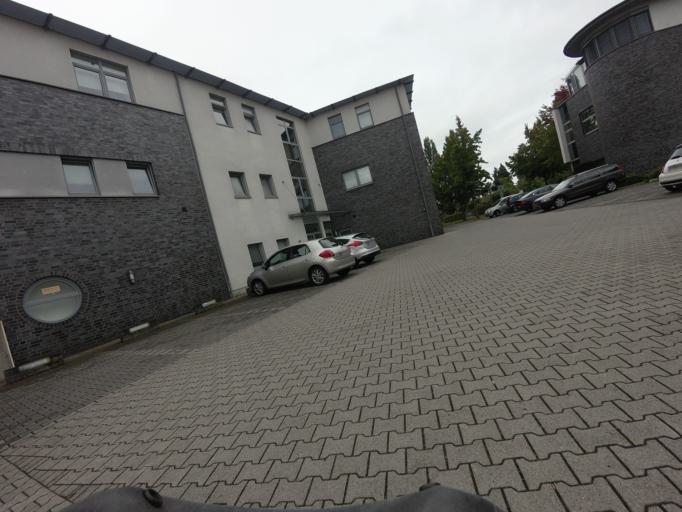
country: DE
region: North Rhine-Westphalia
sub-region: Regierungsbezirk Munster
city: Gronau
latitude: 52.2119
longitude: 7.0288
